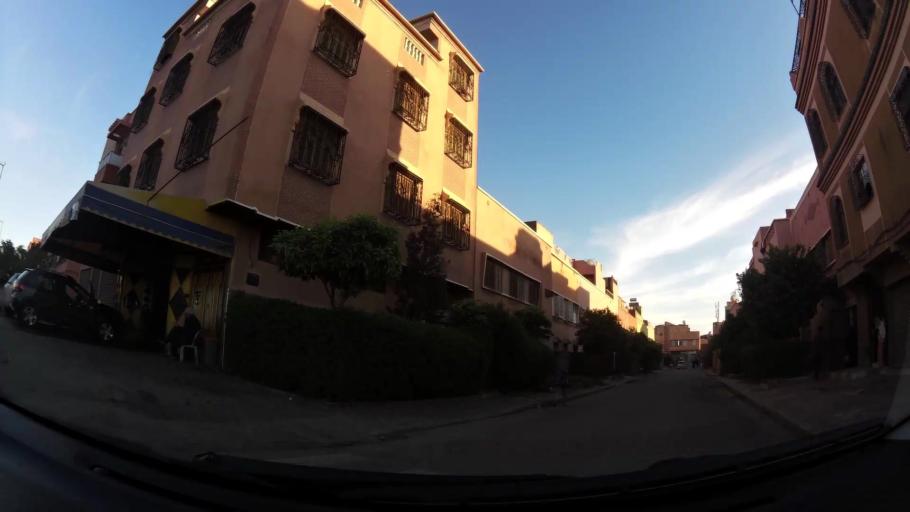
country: MA
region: Marrakech-Tensift-Al Haouz
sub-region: Marrakech
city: Marrakesh
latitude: 31.6260
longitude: -8.0350
